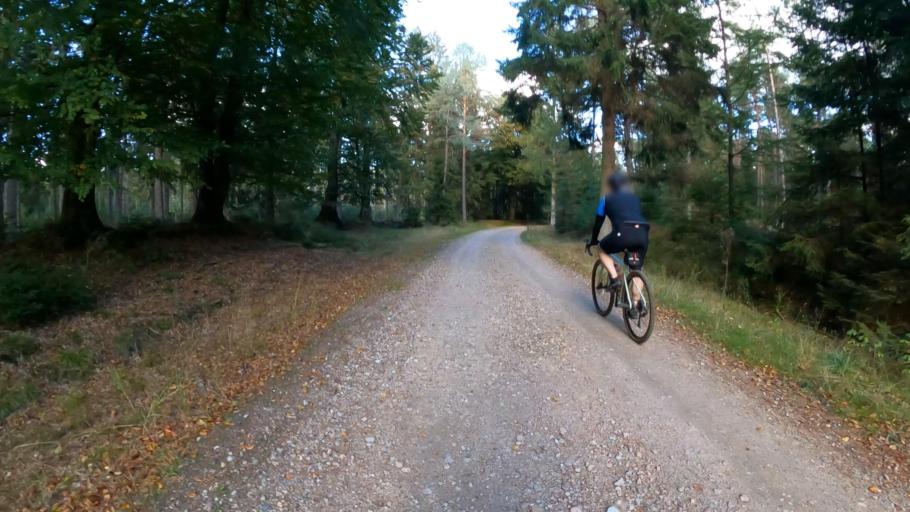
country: DE
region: Schleswig-Holstein
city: Heidmuhlen
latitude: 53.9446
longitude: 10.1010
